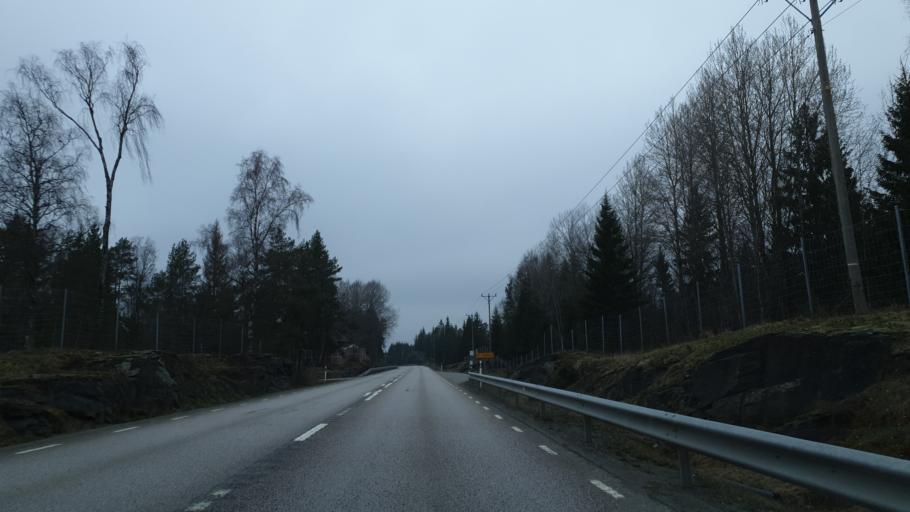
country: SE
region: Vaestra Goetaland
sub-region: Harryda Kommun
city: Hindas
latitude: 57.6345
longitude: 12.4096
